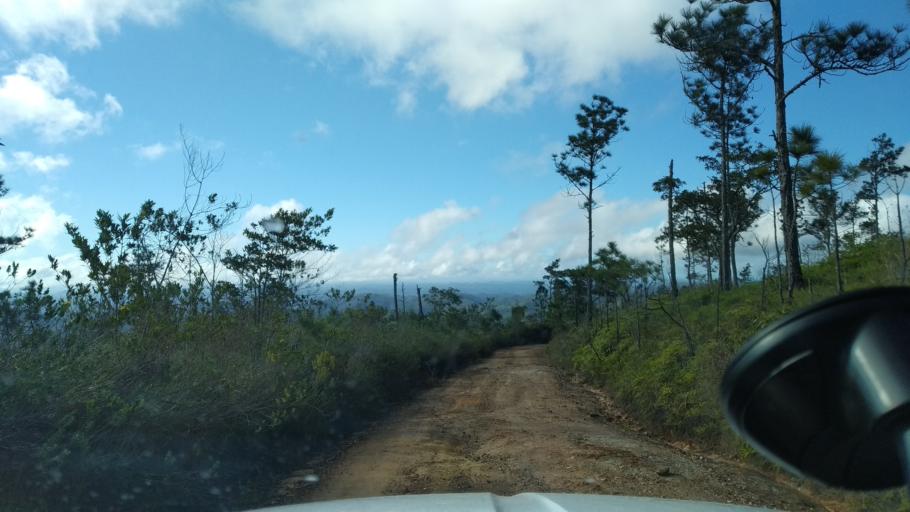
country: BZ
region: Cayo
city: Belmopan
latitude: 16.9976
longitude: -88.8326
